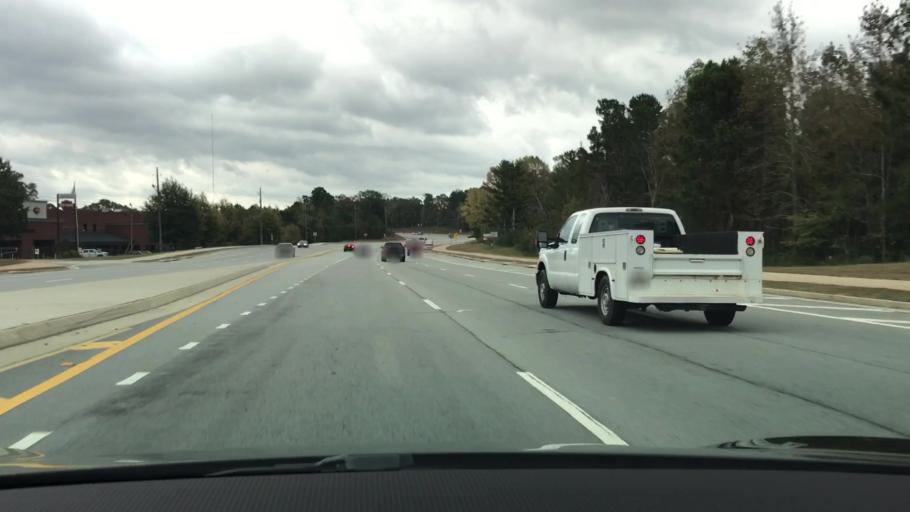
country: US
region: Georgia
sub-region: Hall County
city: Flowery Branch
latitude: 34.1386
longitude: -83.9483
